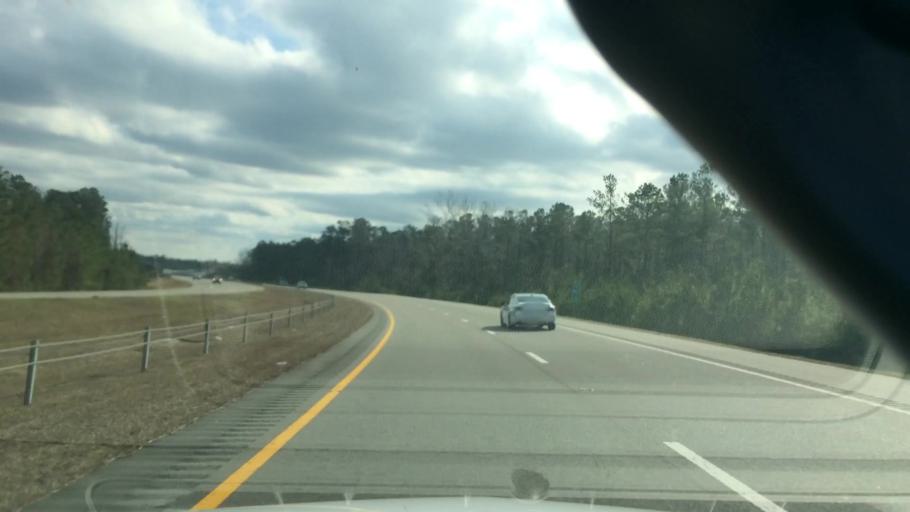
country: US
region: North Carolina
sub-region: Brunswick County
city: Leland
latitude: 34.2001
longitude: -78.0836
